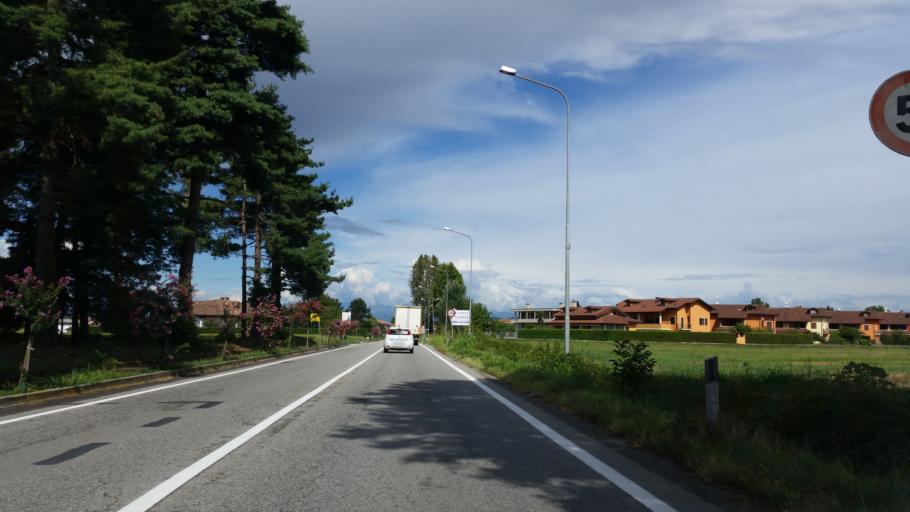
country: IT
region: Piedmont
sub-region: Provincia di Torino
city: Marocchi
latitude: 44.9393
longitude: 7.8224
